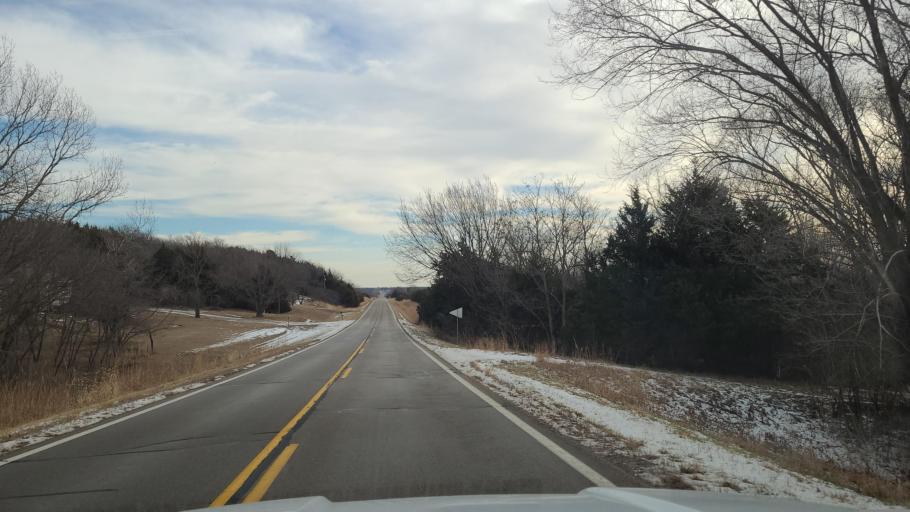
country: US
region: Kansas
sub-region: Jefferson County
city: Oskaloosa
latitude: 39.0437
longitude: -95.4372
